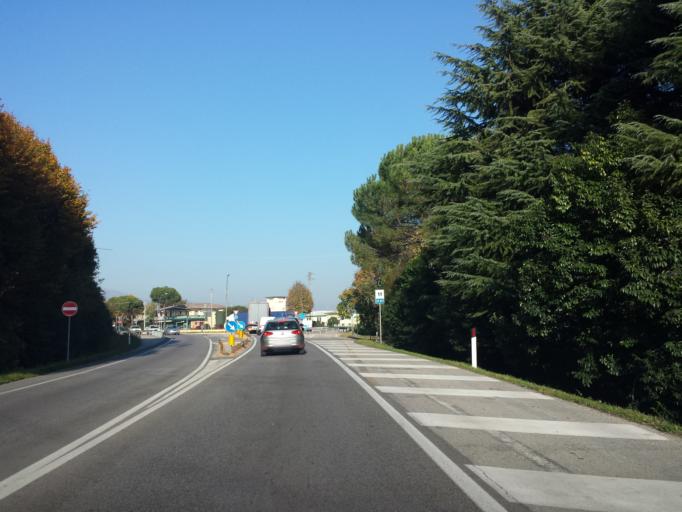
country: IT
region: Veneto
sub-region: Provincia di Treviso
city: Caselle
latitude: 45.7623
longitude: 11.9945
